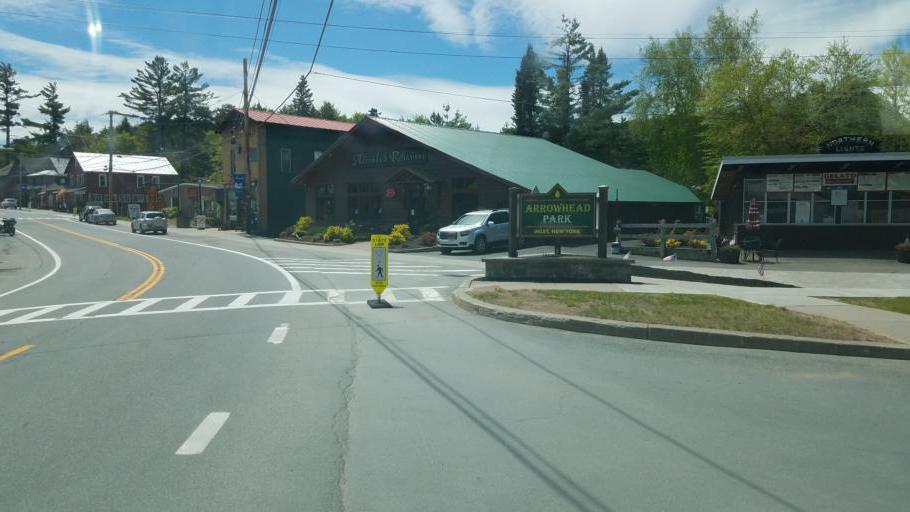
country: US
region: New York
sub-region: Hamilton County
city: Lake Pleasant
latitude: 43.7519
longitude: -74.7946
